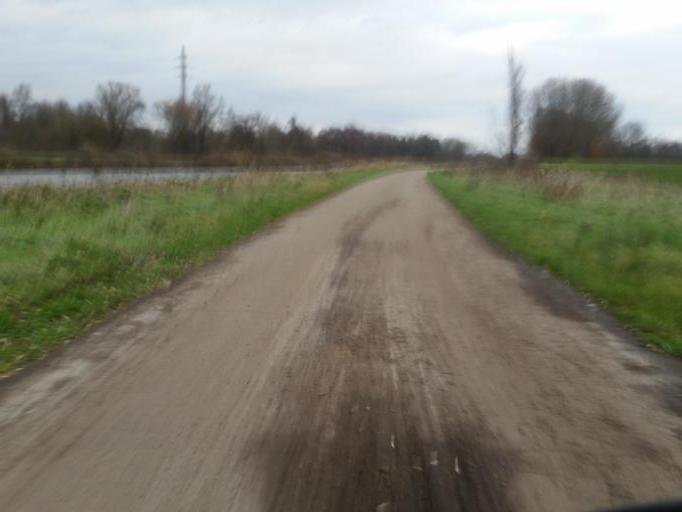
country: BE
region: Flanders
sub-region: Provincie Antwerpen
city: Lier
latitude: 51.1515
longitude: 4.5872
